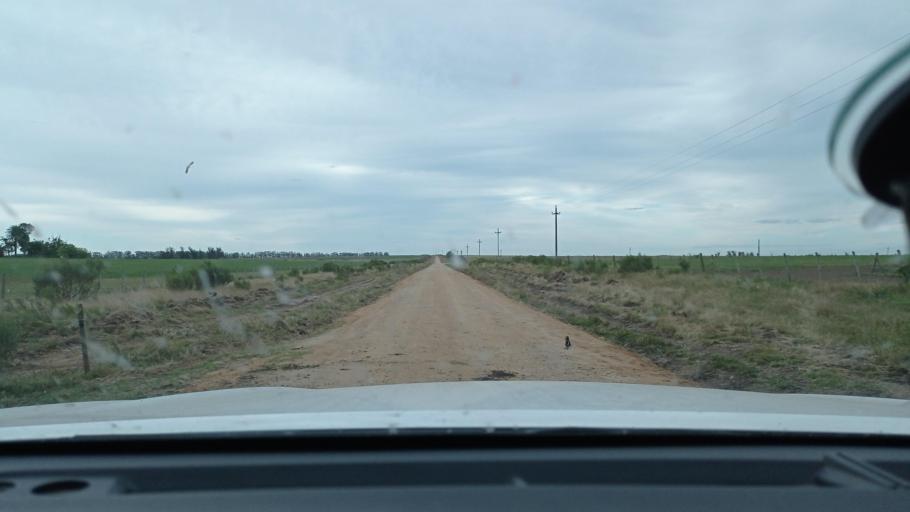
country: UY
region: Florida
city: Casupa
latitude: -34.1072
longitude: -55.7640
